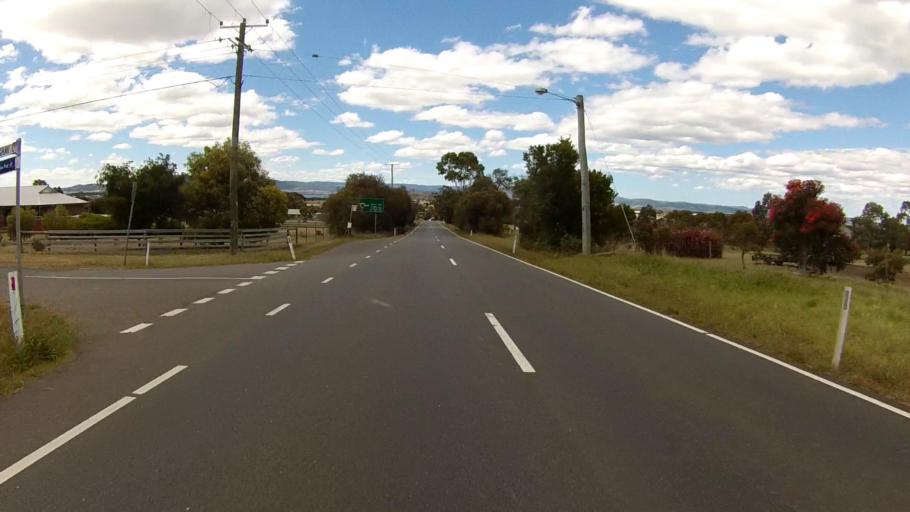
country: AU
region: Tasmania
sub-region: Clarence
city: Seven Mile Beach
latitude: -42.8505
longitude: 147.4755
